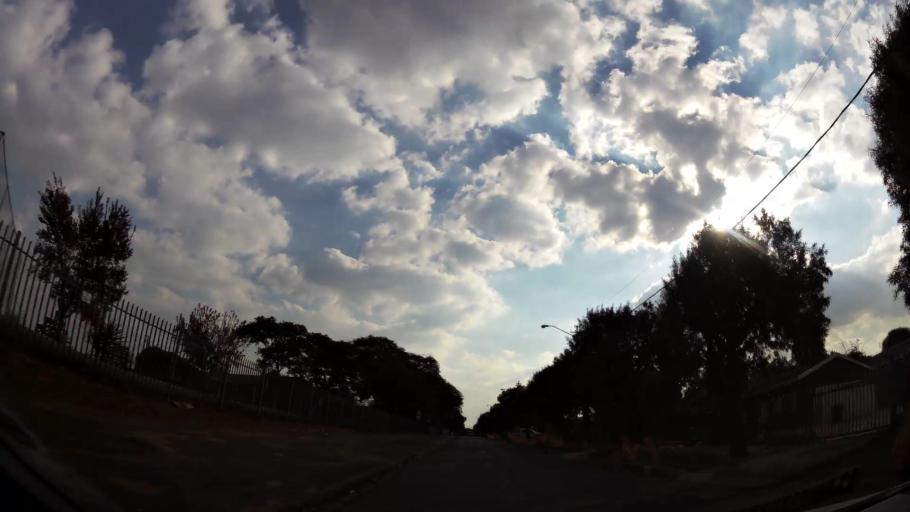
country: ZA
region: Gauteng
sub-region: Ekurhuleni Metropolitan Municipality
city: Germiston
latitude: -26.2421
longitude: 28.1854
